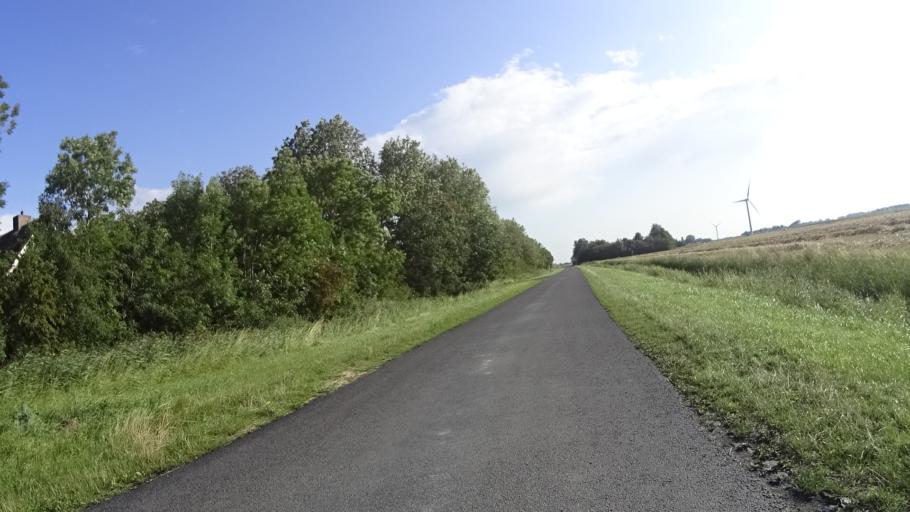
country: NL
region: Friesland
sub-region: Sudwest Fryslan
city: Makkum
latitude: 53.1146
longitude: 5.4122
